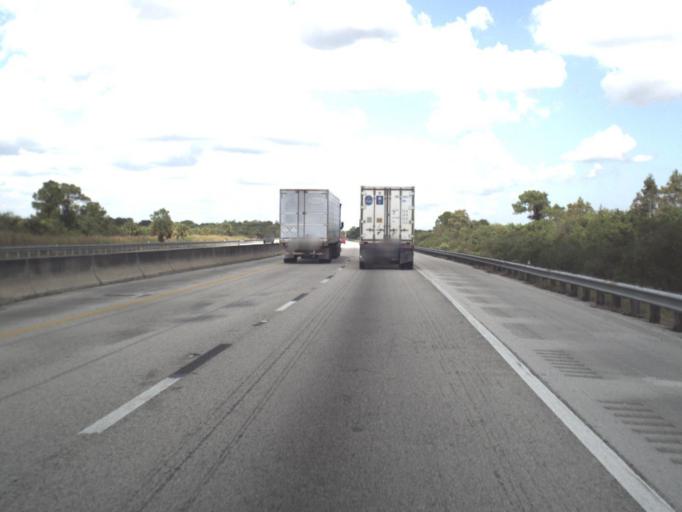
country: US
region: Florida
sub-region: Martin County
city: Port Salerno
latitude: 27.0593
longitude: -80.2411
